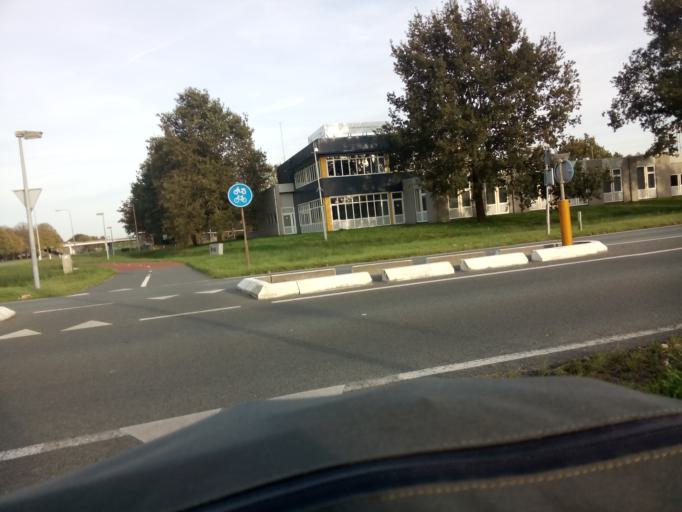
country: NL
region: Drenthe
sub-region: Gemeente Assen
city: Assen
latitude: 52.9963
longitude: 6.5208
